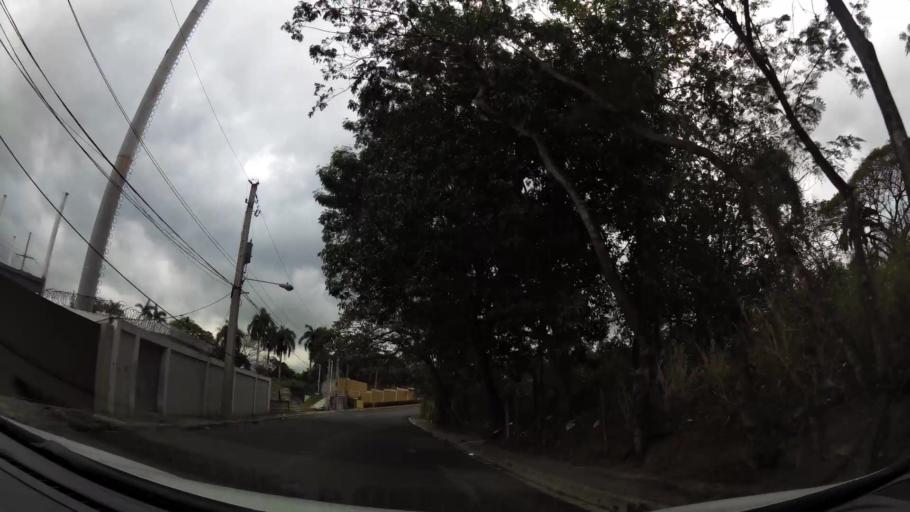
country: DO
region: Nacional
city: Santo Domingo
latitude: 18.5066
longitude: -69.9720
